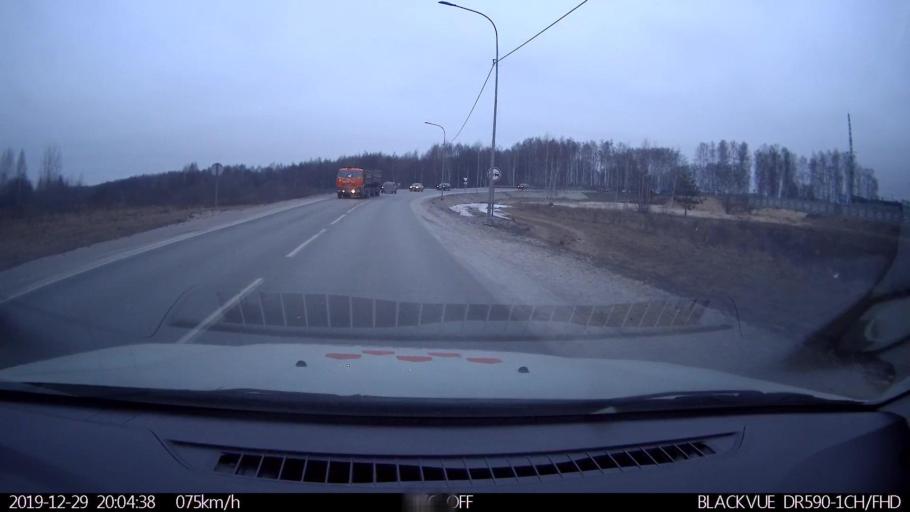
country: RU
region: Nizjnij Novgorod
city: Neklyudovo
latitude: 56.3860
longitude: 44.0092
